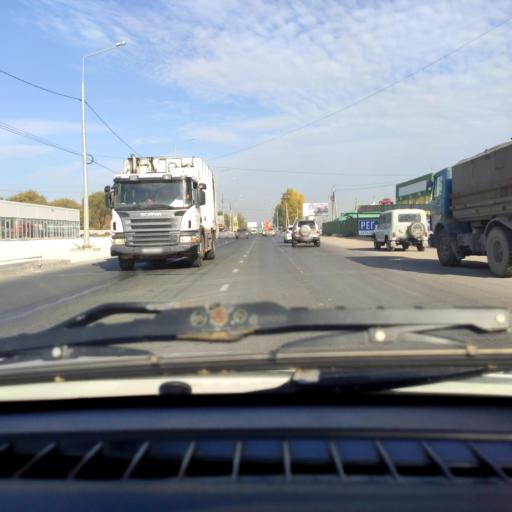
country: RU
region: Samara
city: Tol'yatti
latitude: 53.5692
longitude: 49.4587
